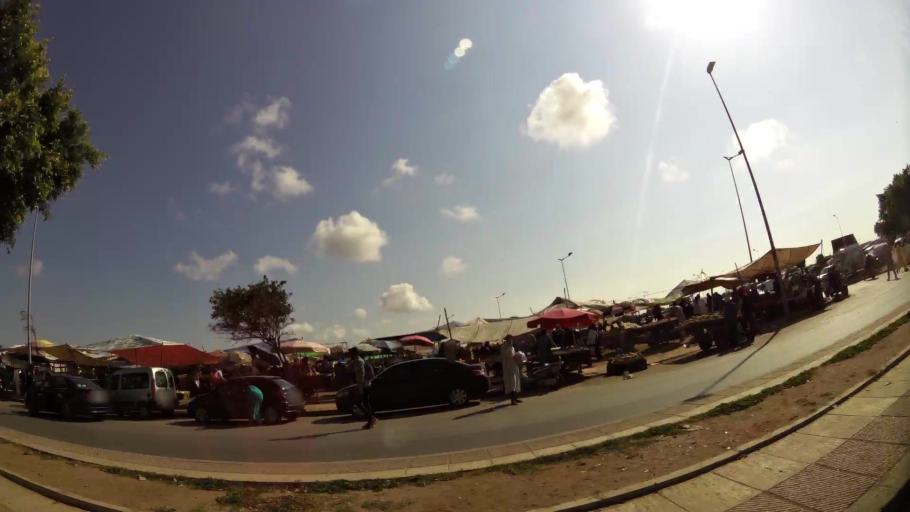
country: MA
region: Rabat-Sale-Zemmour-Zaer
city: Sale
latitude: 34.0503
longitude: -6.7893
